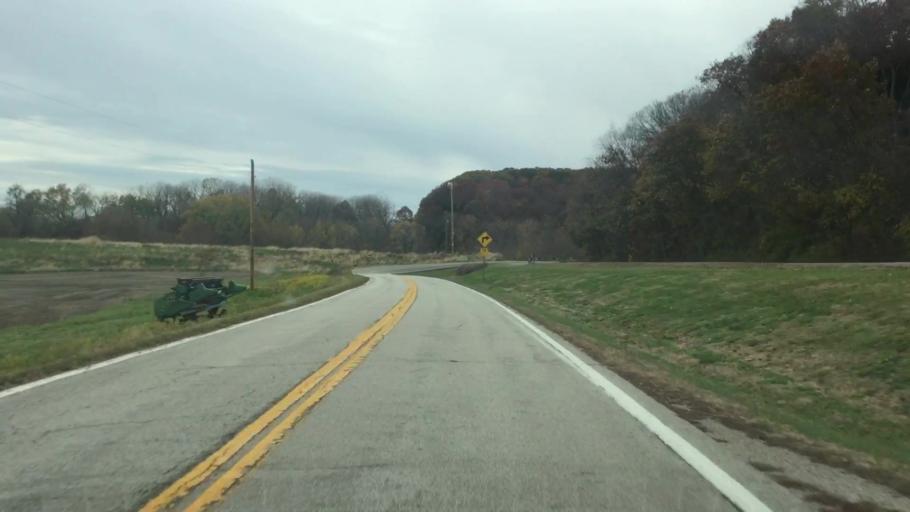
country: US
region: Missouri
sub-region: Gasconade County
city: Hermann
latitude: 38.7054
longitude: -91.6223
